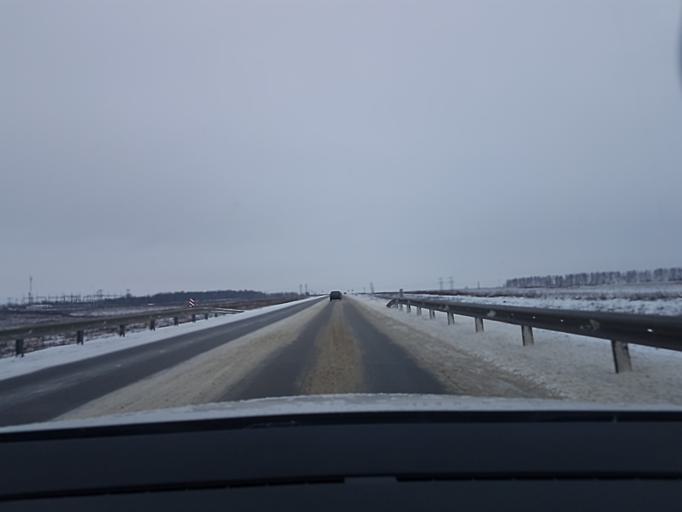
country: RU
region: Rjazan
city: Skopin
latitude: 53.9568
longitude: 39.4343
